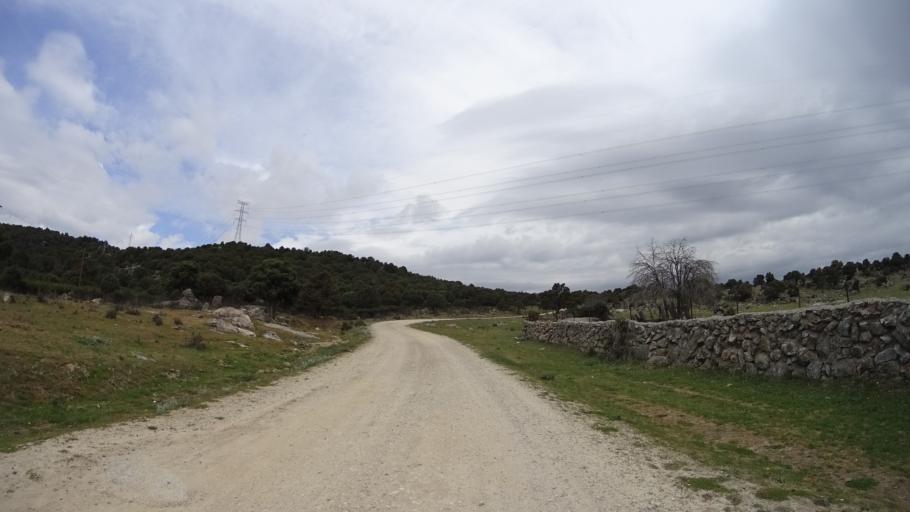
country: ES
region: Madrid
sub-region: Provincia de Madrid
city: Hoyo de Manzanares
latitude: 40.6131
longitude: -3.8786
